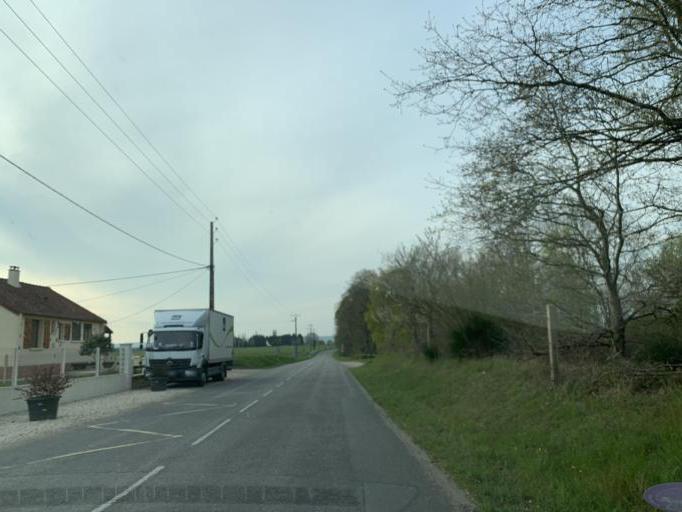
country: FR
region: Haute-Normandie
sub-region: Departement de la Seine-Maritime
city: La Mailleraye-sur-Seine
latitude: 49.4883
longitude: 0.7681
